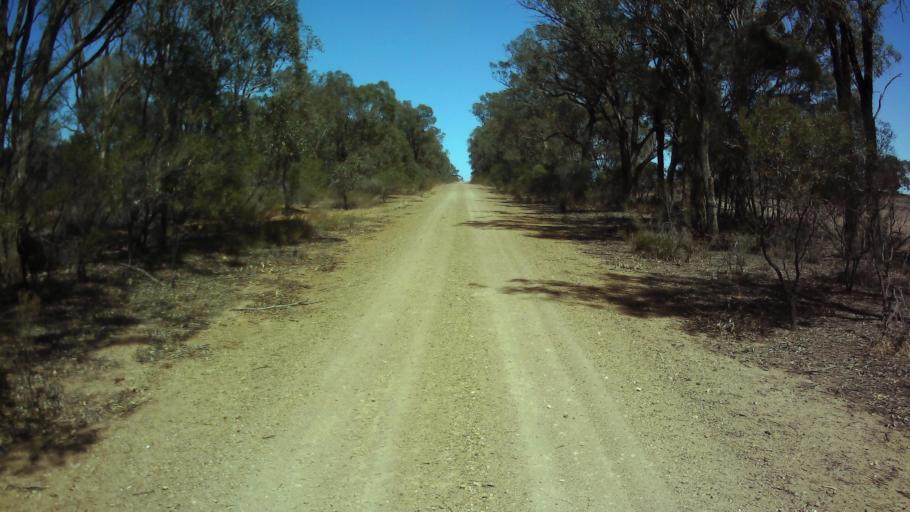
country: AU
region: New South Wales
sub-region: Forbes
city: Forbes
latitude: -33.6957
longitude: 147.8402
